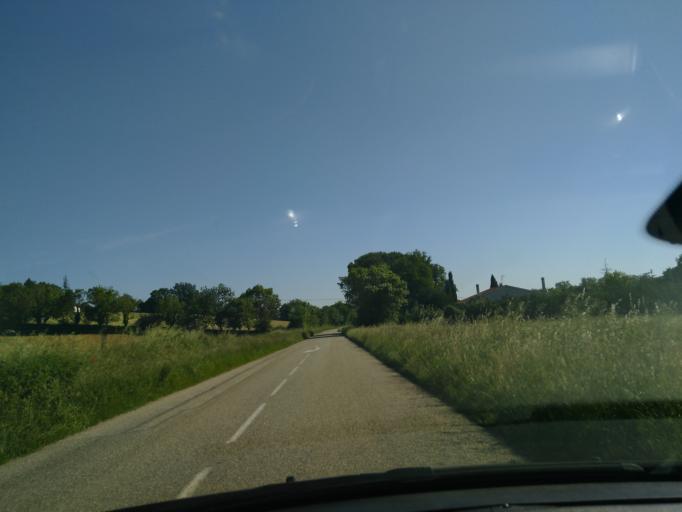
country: FR
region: Midi-Pyrenees
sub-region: Departement du Gers
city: Gimont
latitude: 43.5988
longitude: 0.8418
